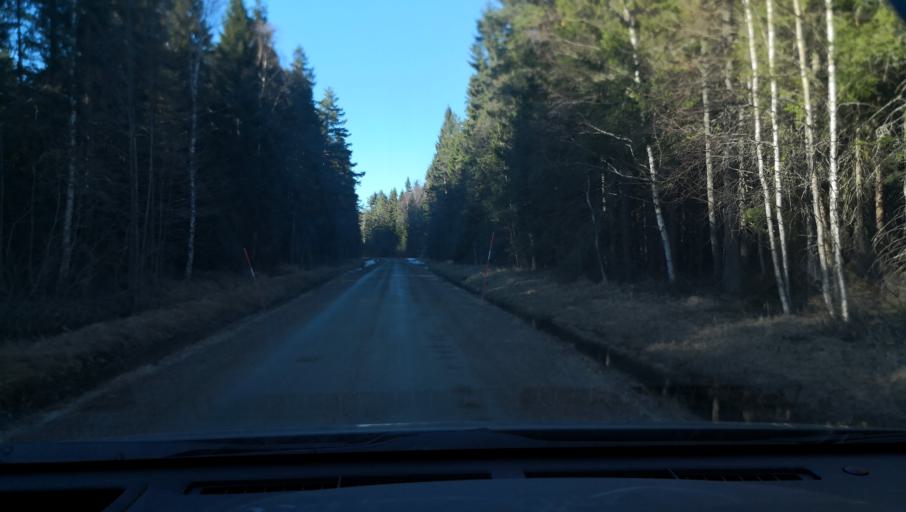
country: SE
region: Vaestmanland
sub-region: Sala Kommun
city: Sala
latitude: 60.1410
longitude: 16.6488
